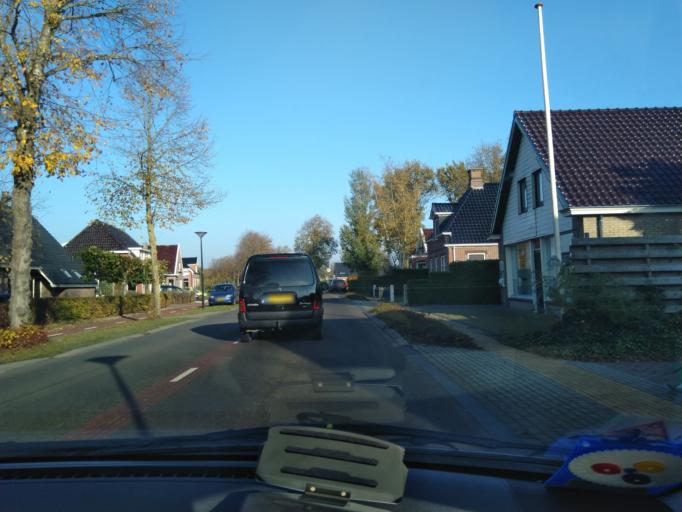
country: NL
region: Drenthe
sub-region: Gemeente Tynaarlo
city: Zuidlaren
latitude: 53.1120
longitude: 6.7127
